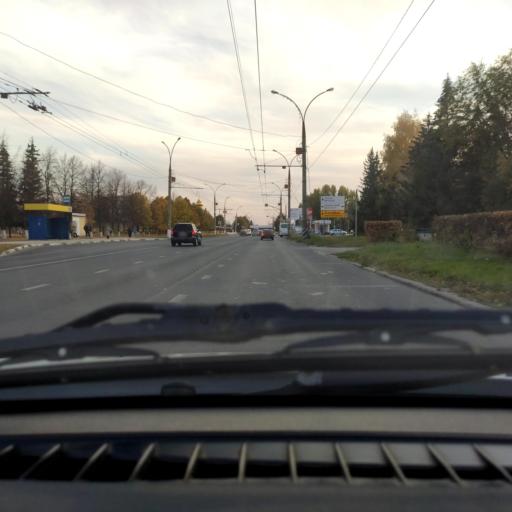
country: RU
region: Samara
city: Tol'yatti
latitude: 53.5222
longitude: 49.2742
